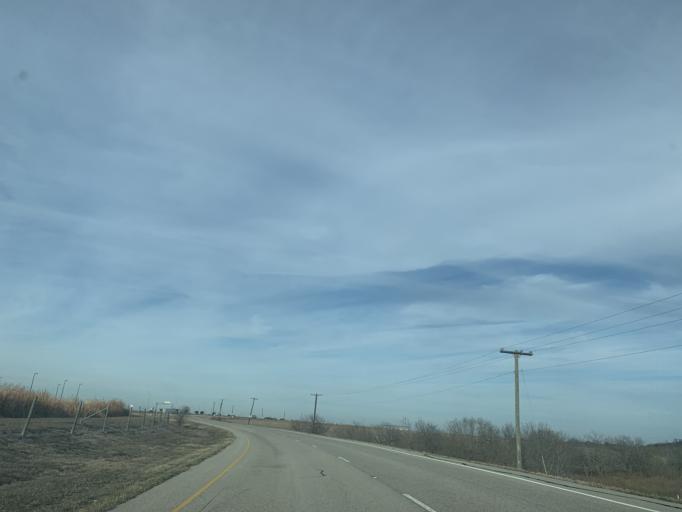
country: US
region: Texas
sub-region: Bell County
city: Salado
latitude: 30.9033
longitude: -97.5566
